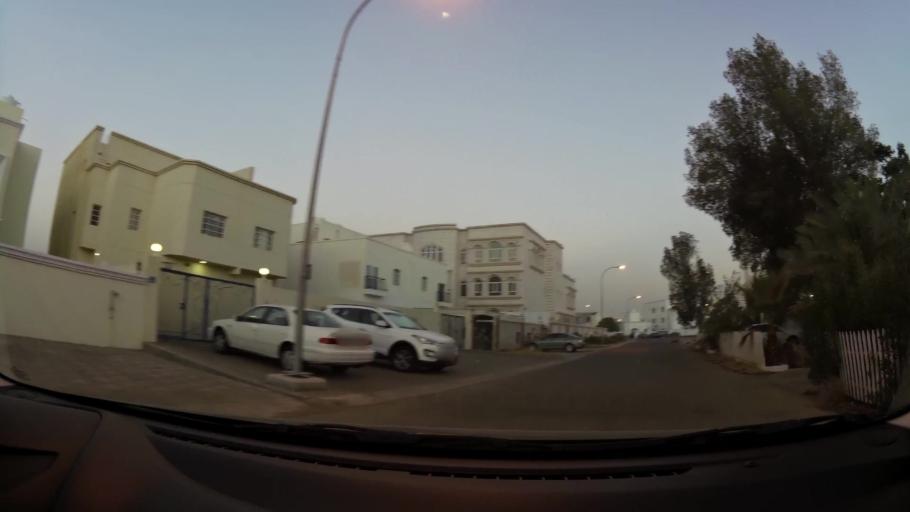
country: OM
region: Muhafazat Masqat
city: As Sib al Jadidah
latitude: 23.6028
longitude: 58.2368
